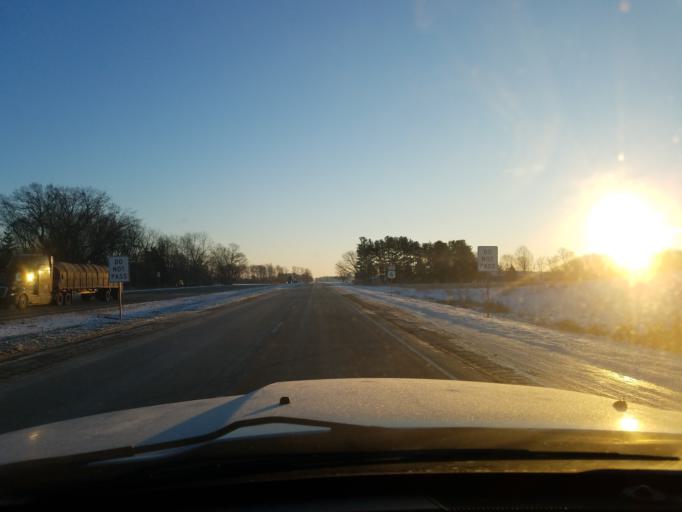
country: US
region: Indiana
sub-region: Marshall County
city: Plymouth
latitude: 41.4498
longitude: -86.2896
